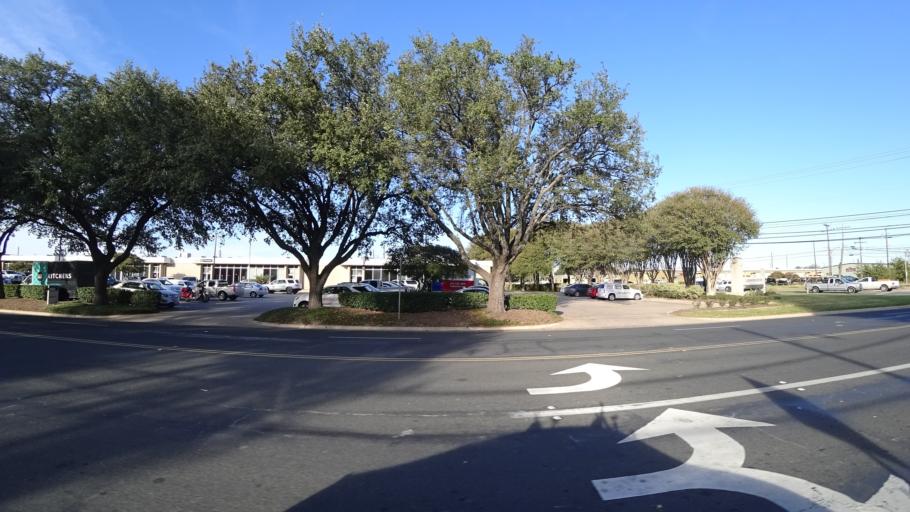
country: US
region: Texas
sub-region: Williamson County
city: Jollyville
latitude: 30.3802
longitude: -97.7255
